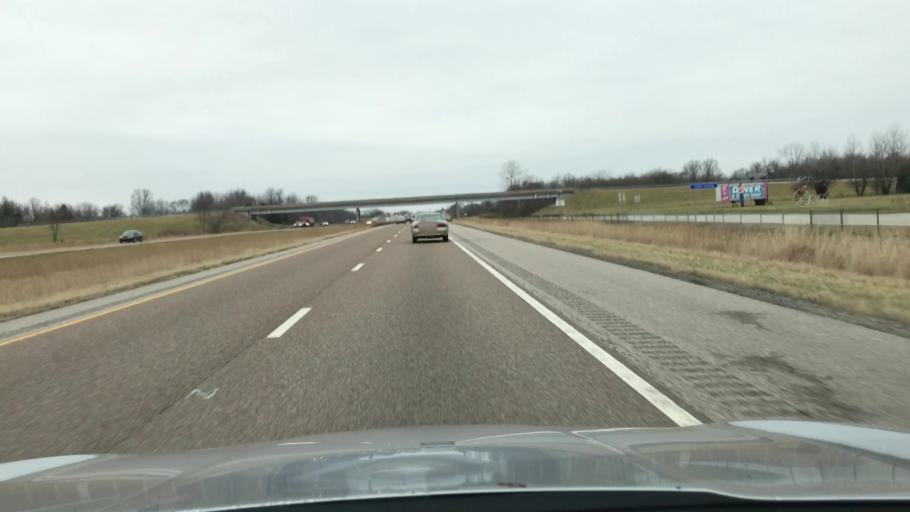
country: US
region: Illinois
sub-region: Macoupin County
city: Staunton
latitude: 38.9602
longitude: -89.7635
